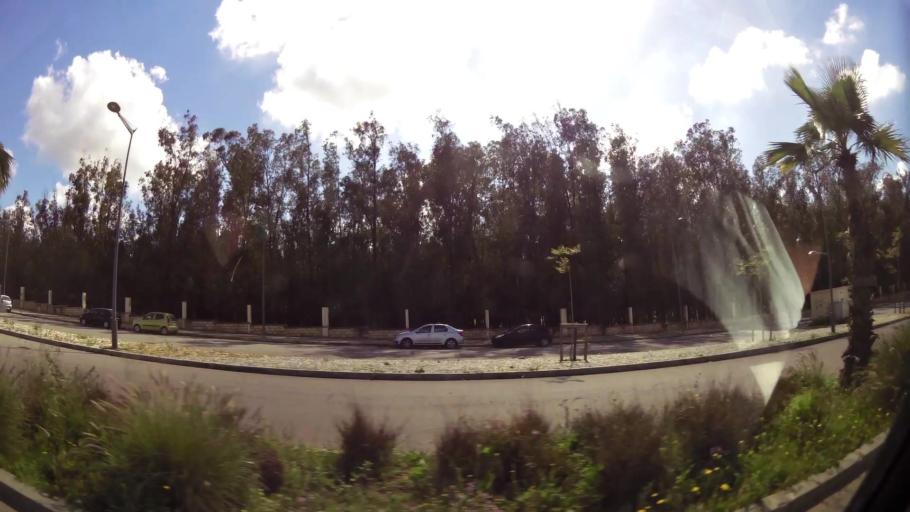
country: MA
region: Grand Casablanca
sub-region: Nouaceur
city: Bouskoura
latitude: 33.4735
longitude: -7.6166
